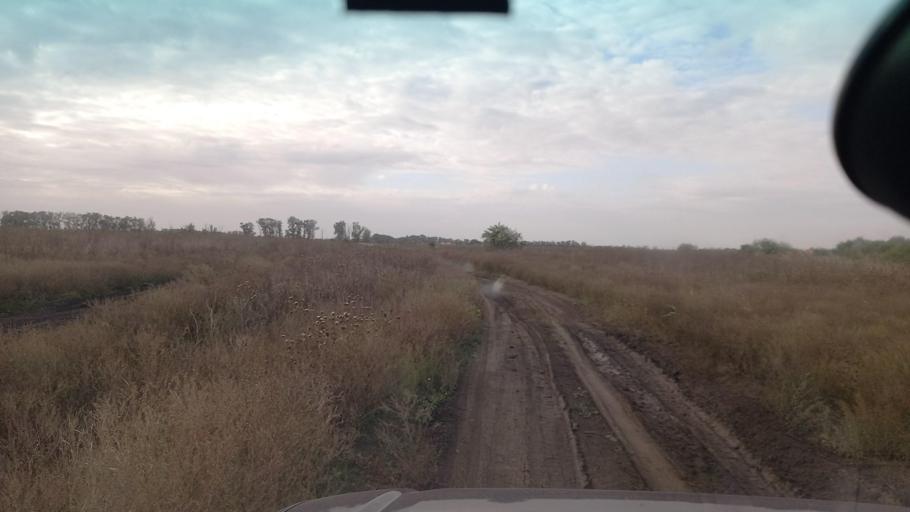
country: RU
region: Krasnodarskiy
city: Krasnodar
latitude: 45.1321
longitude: 38.9285
